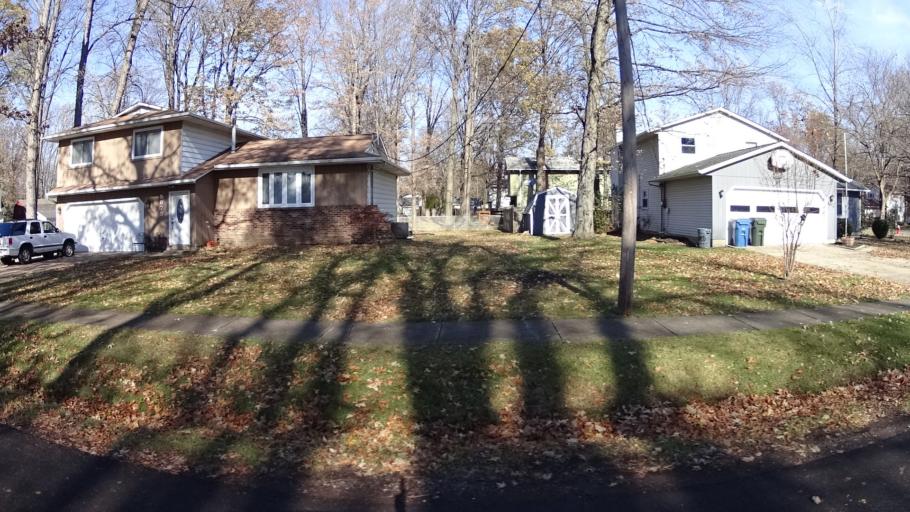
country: US
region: Ohio
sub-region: Lorain County
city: Sheffield Lake
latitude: 41.4900
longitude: -82.0815
